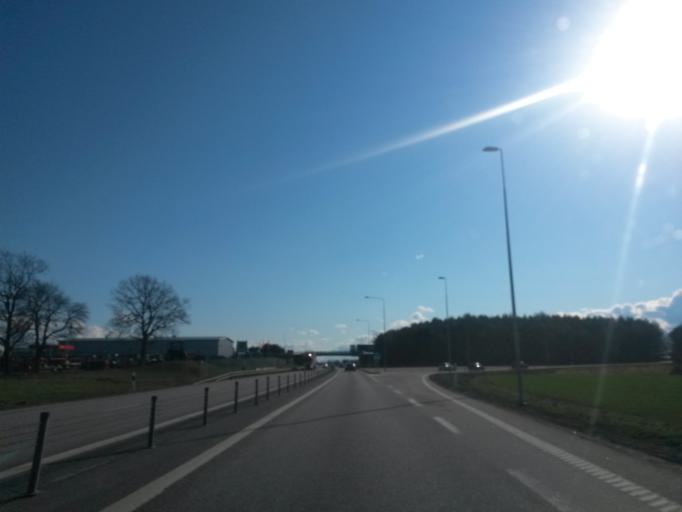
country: SE
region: Vaestra Goetaland
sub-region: Vara Kommun
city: Vara
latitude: 58.2805
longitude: 13.0216
